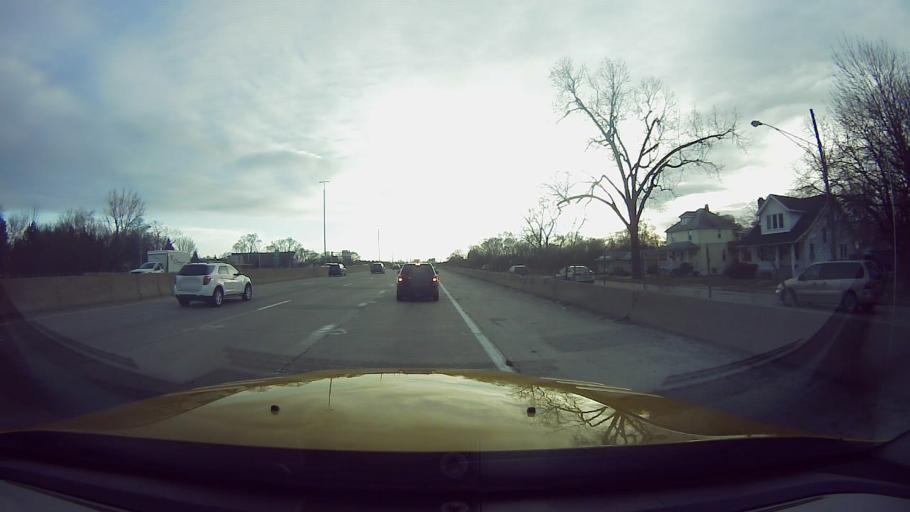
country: US
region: Michigan
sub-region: Wayne County
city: Allen Park
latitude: 42.2748
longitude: -83.2199
